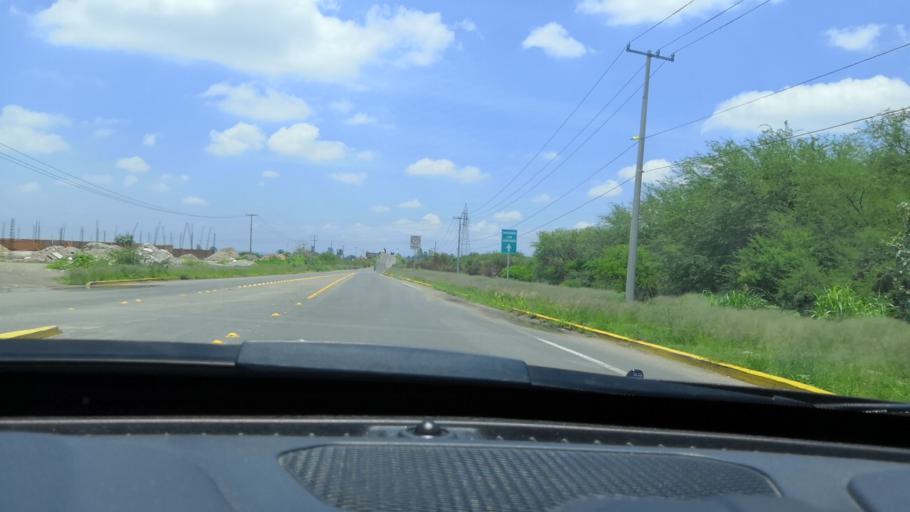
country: MX
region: Guanajuato
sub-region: Silao de la Victoria
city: El Refugio de los Sauces
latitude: 21.0152
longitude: -101.5793
